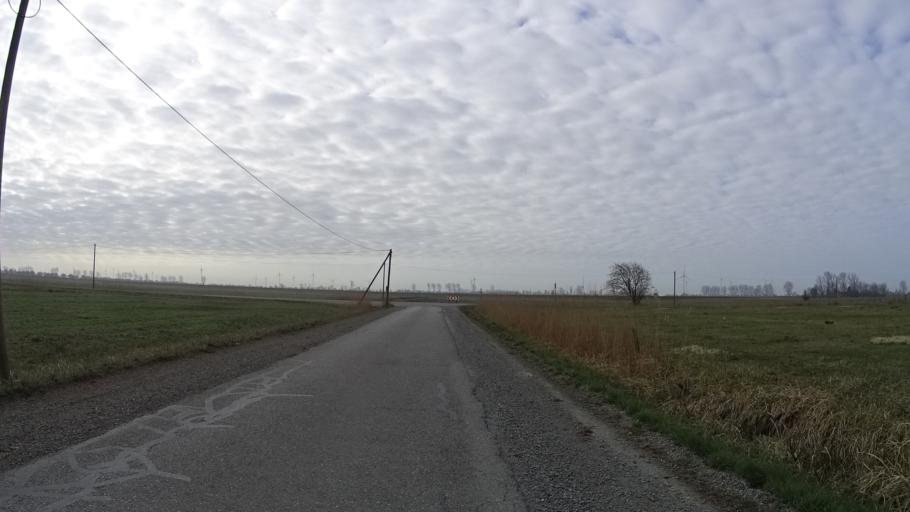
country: DE
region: Lower Saxony
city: Emden
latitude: 53.4037
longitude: 7.3066
